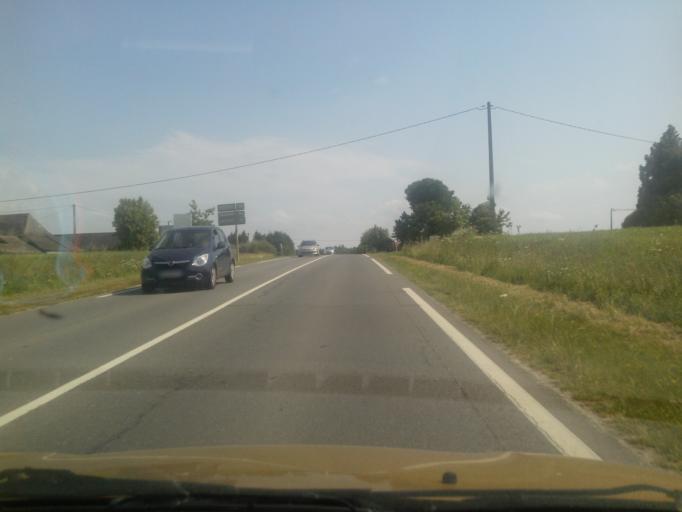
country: FR
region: Brittany
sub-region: Departement d'Ille-et-Vilaine
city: Melesse
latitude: 48.2096
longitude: -1.6990
